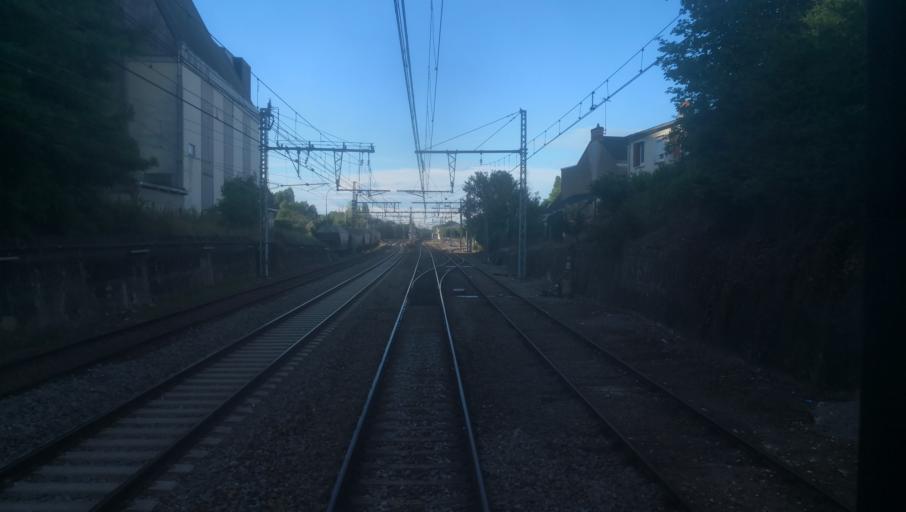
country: FR
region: Centre
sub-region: Departement de l'Indre
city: Issoudun
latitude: 46.9442
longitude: 1.9830
